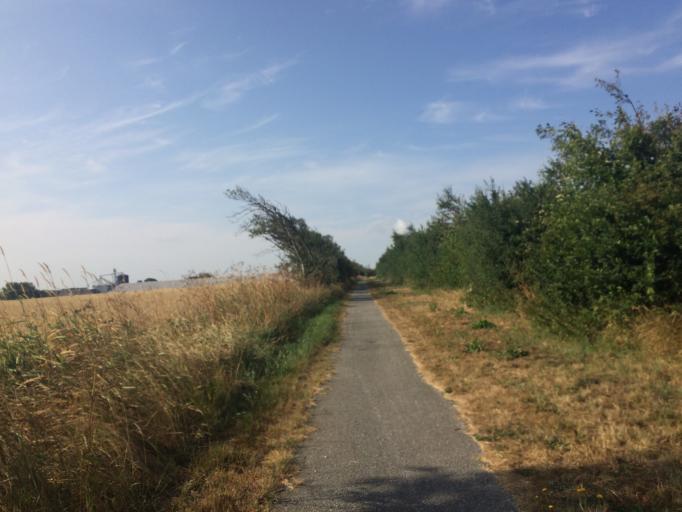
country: DK
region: Central Jutland
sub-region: Holstebro Kommune
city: Vinderup
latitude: 56.6318
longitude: 8.7854
